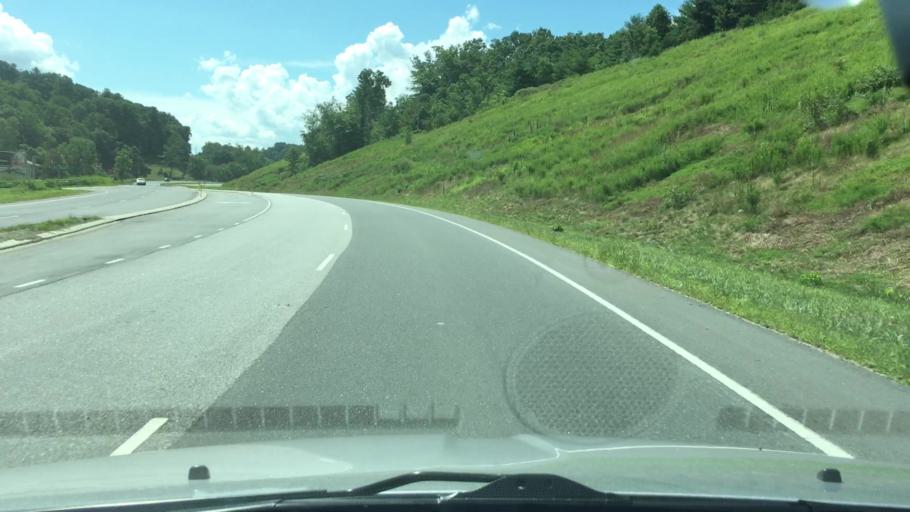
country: US
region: North Carolina
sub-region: Yancey County
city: Burnsville
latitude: 35.9152
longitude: -82.2387
